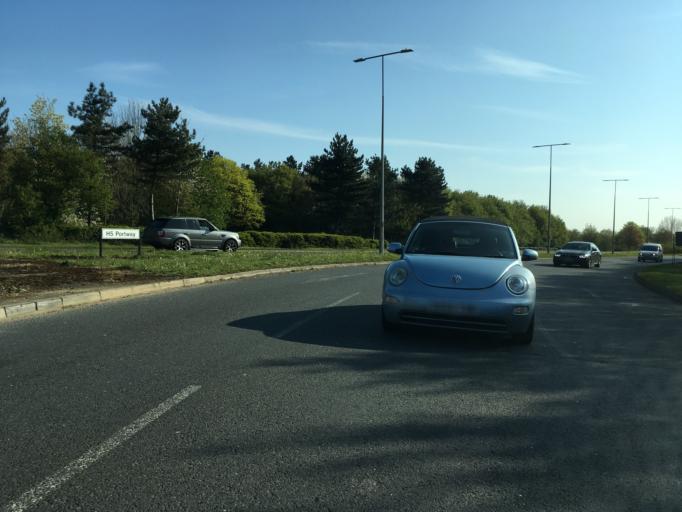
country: GB
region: England
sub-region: Milton Keynes
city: Milton Keynes
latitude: 52.0544
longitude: -0.7277
